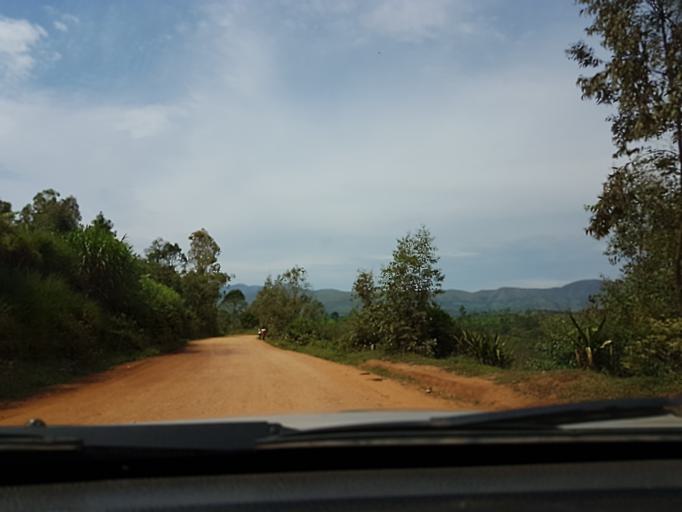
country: CD
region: South Kivu
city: Bukavu
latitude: -2.6243
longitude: 28.8753
